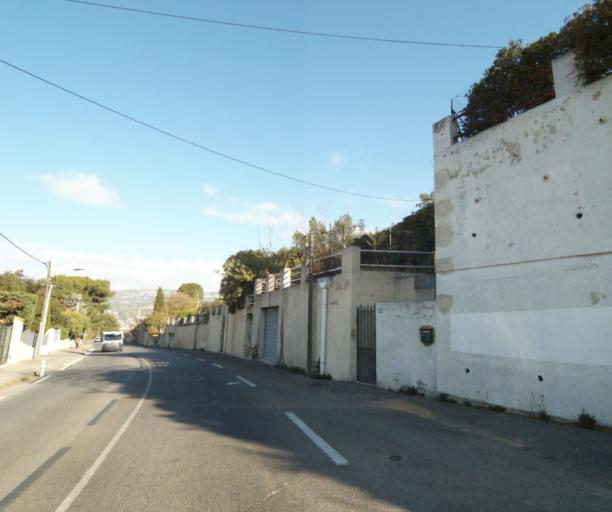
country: FR
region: Provence-Alpes-Cote d'Azur
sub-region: Departement des Bouches-du-Rhone
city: Allauch
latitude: 43.3421
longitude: 5.4861
